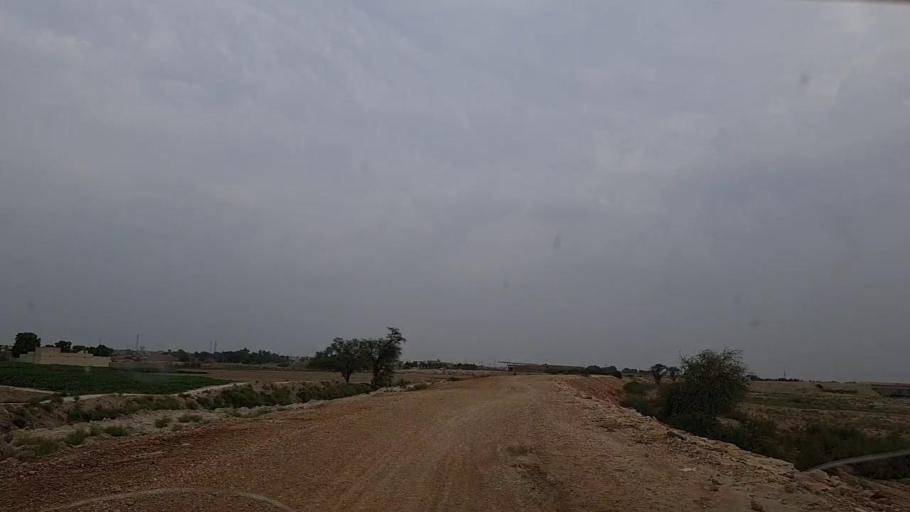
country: PK
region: Sindh
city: Johi
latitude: 26.7015
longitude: 67.5980
